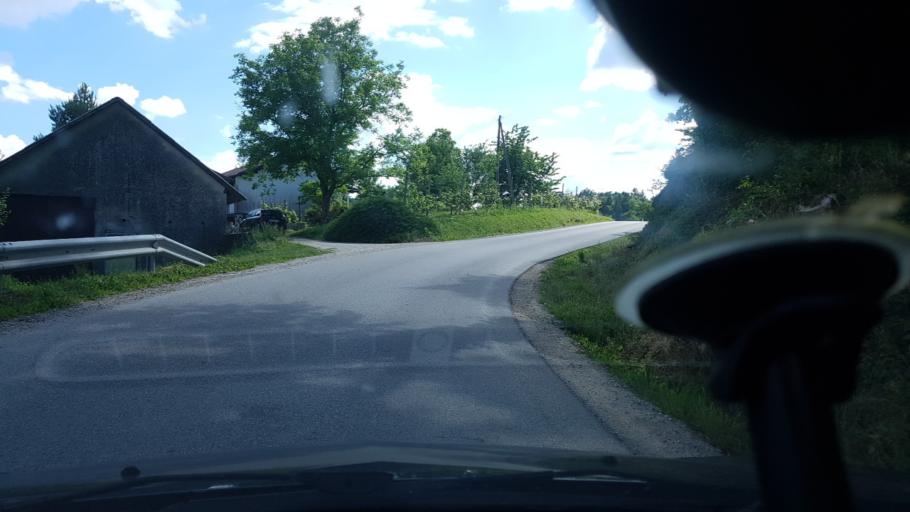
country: SI
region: Rogatec
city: Rogatec
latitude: 46.2464
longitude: 15.7251
